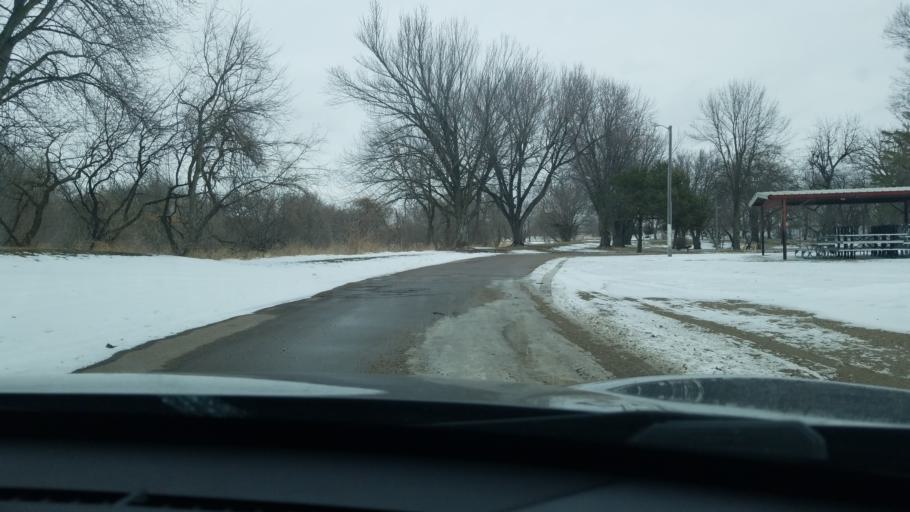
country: US
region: Iowa
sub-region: Lyon County
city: Rock Rapids
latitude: 43.4357
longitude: -96.1688
